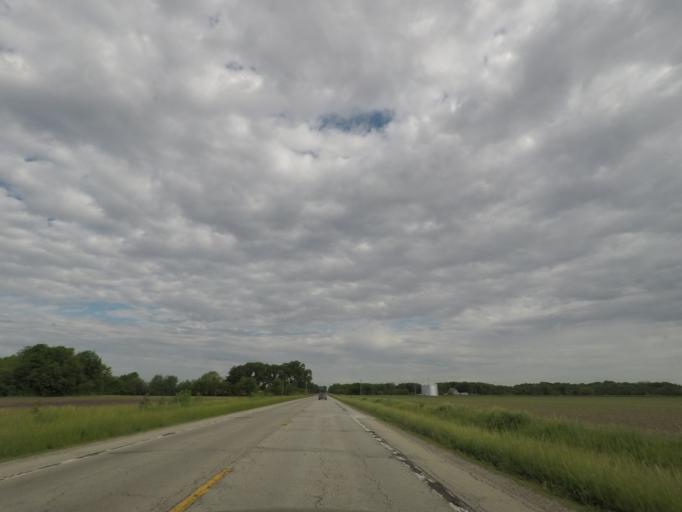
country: US
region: Illinois
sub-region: Logan County
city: Lincoln
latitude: 40.1118
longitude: -89.3285
